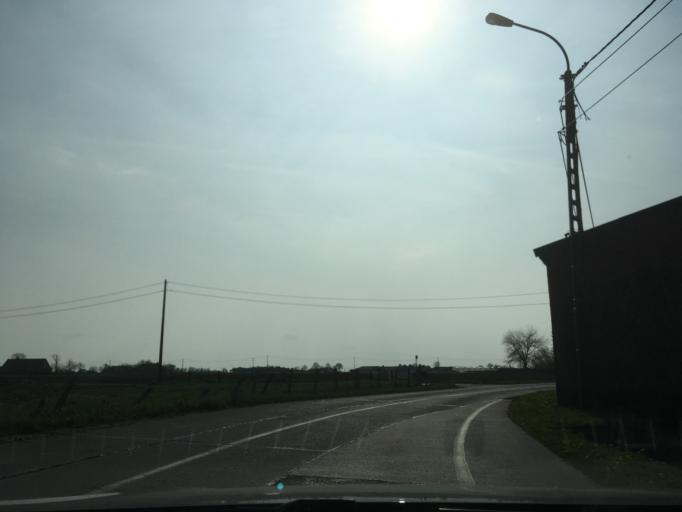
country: BE
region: Flanders
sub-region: Provincie West-Vlaanderen
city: Lichtervelde
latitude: 51.0265
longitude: 3.1896
